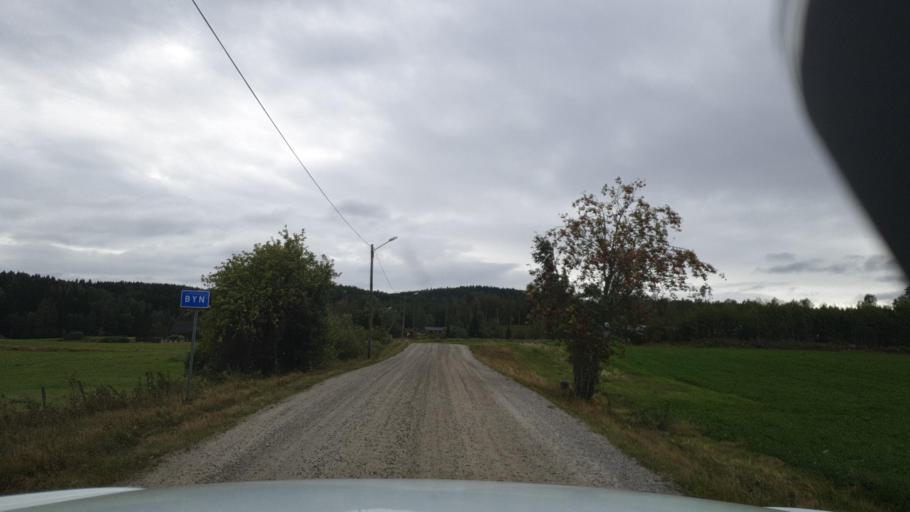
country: SE
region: Vaermland
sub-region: Arvika Kommun
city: Arvika
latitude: 59.6691
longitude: 12.7631
